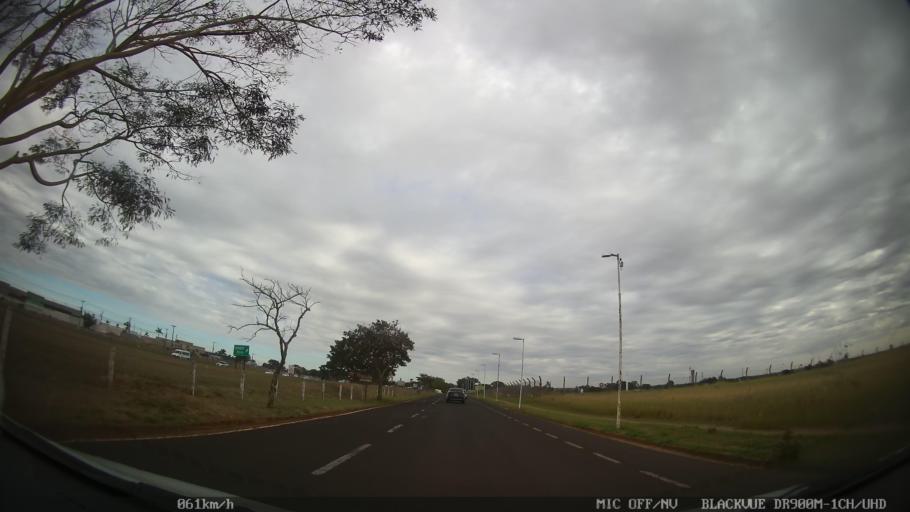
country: BR
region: Sao Paulo
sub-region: Sao Jose Do Rio Preto
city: Sao Jose do Rio Preto
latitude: -20.8234
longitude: -49.4145
